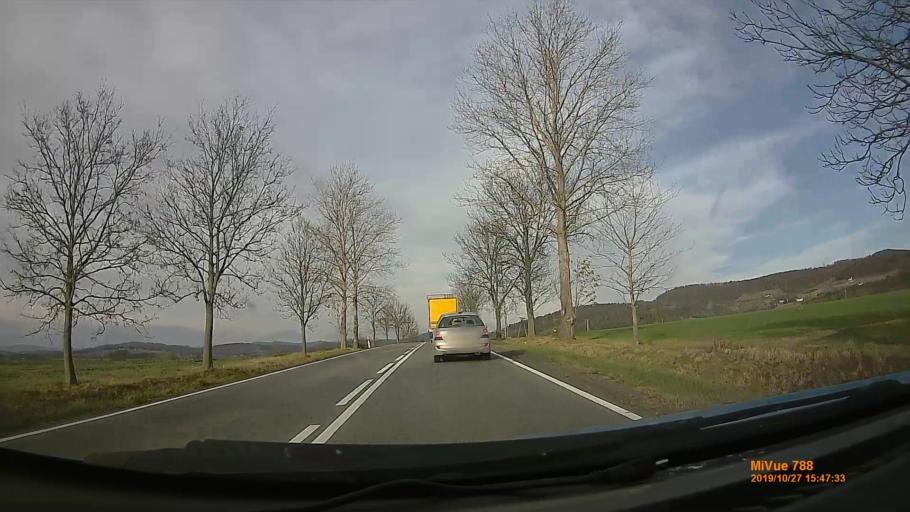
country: PL
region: Lower Silesian Voivodeship
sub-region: Powiat klodzki
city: Bozkow
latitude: 50.4902
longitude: 16.5859
